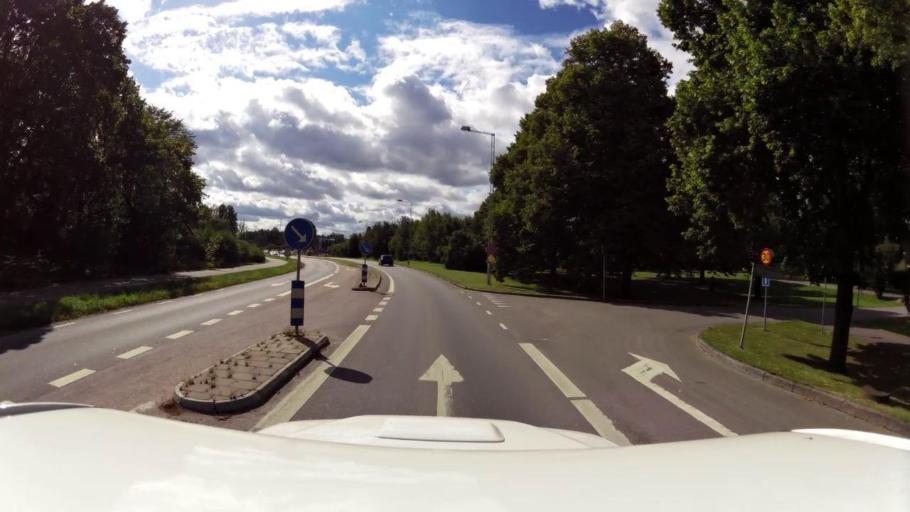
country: SE
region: OEstergoetland
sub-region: Linkopings Kommun
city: Linkoping
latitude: 58.4001
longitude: 15.6088
